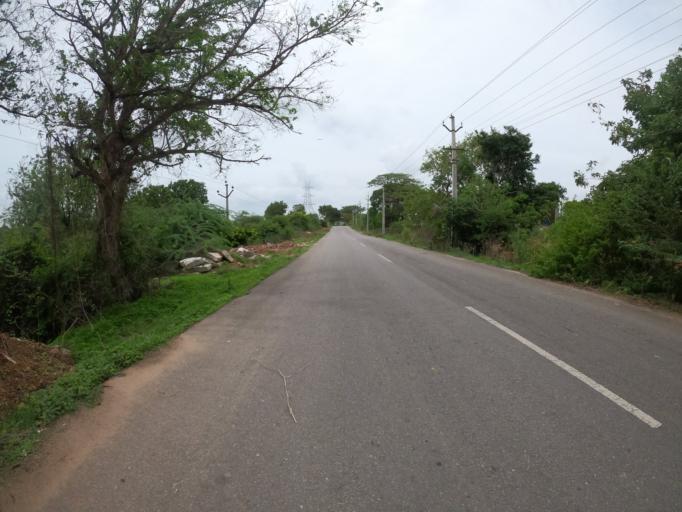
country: IN
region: Telangana
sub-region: Hyderabad
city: Hyderabad
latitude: 17.3437
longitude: 78.3607
